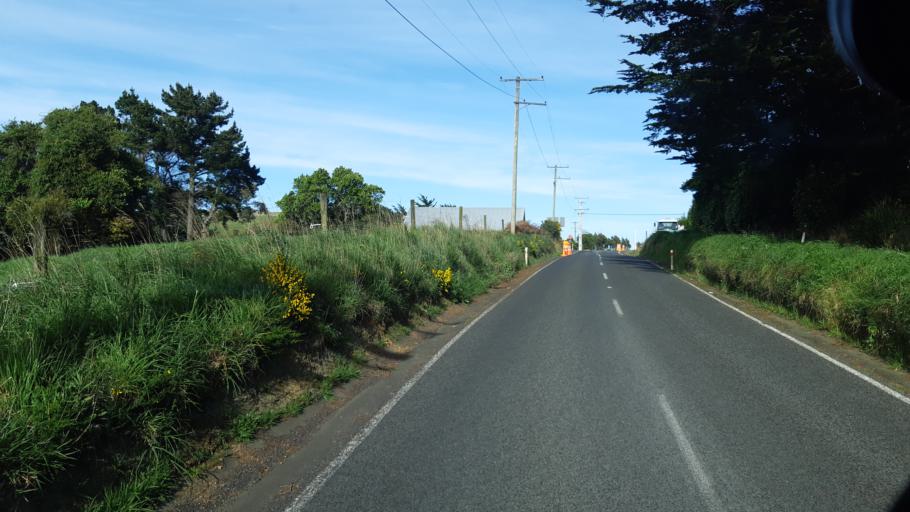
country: NZ
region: Otago
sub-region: Dunedin City
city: Portobello
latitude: -45.8755
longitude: 170.6243
